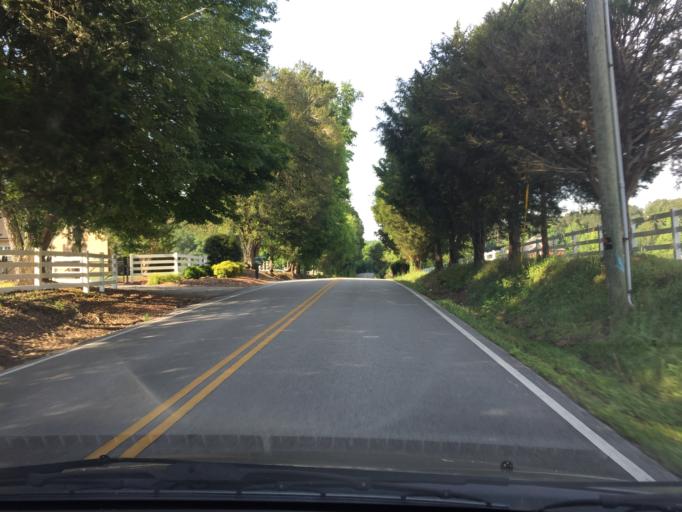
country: US
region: Tennessee
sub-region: Hamilton County
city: Collegedale
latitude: 35.0577
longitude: -85.0161
